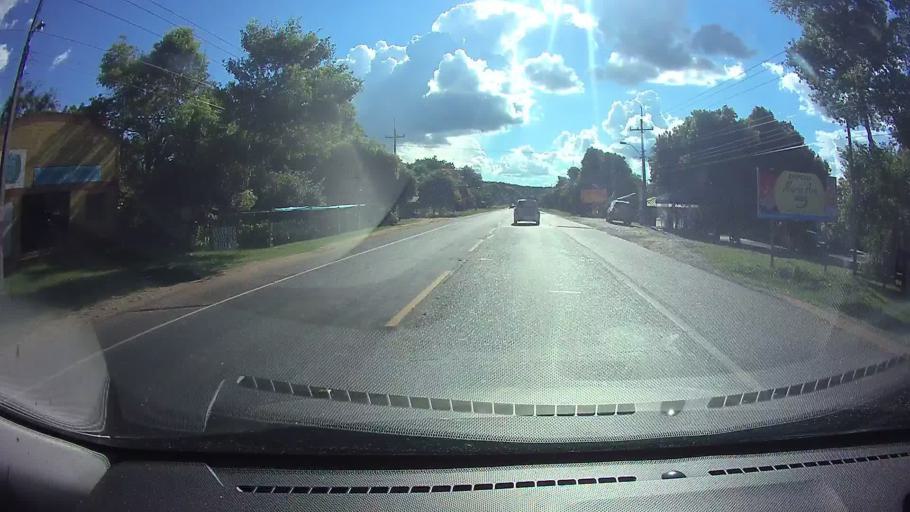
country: PY
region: Cordillera
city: Eusebio Ayala
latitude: -25.3819
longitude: -57.0034
